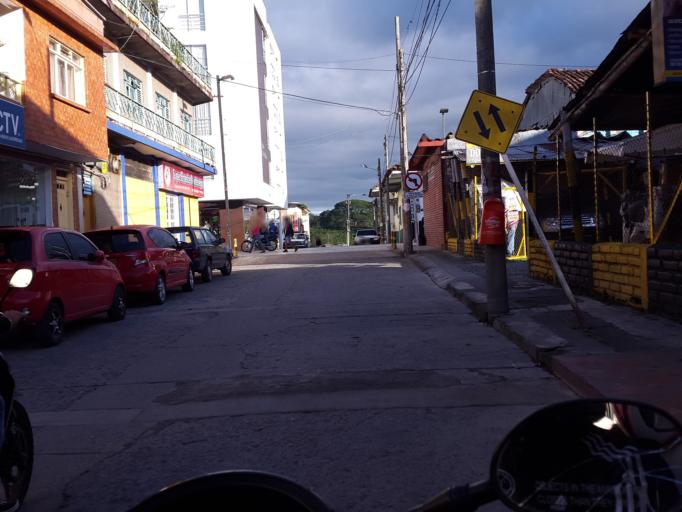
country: CO
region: Quindio
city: Montenegro
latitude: 4.5674
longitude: -75.7496
